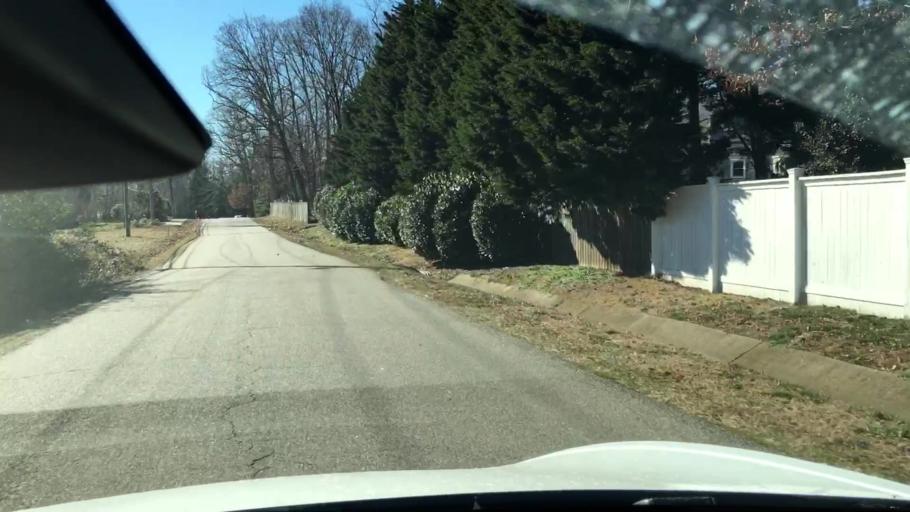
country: US
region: Virginia
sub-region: Chesterfield County
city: Bon Air
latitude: 37.5272
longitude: -77.6009
